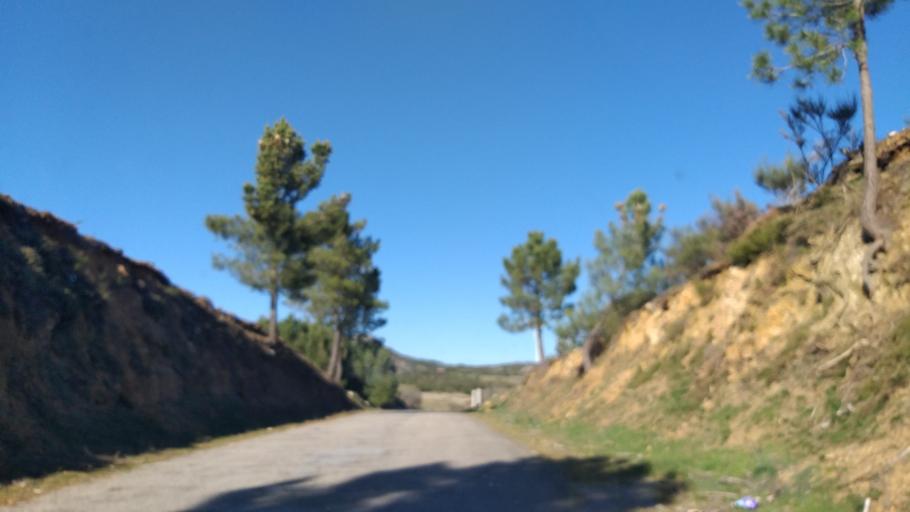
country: PT
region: Guarda
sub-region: Celorico da Beira
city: Celorico da Beira
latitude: 40.5238
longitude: -7.3920
